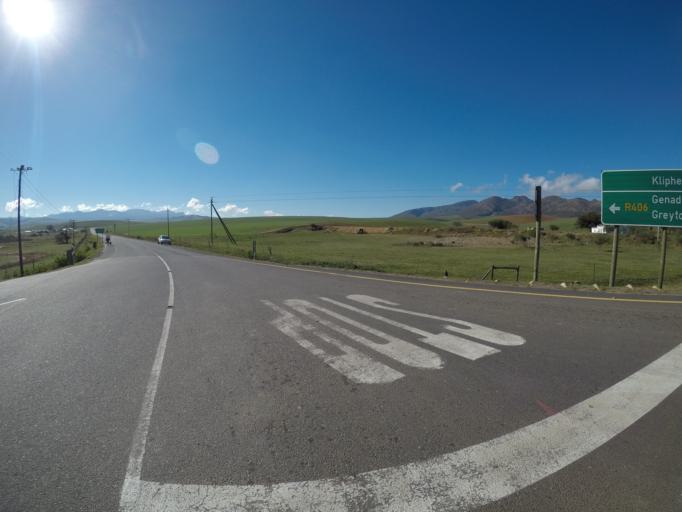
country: ZA
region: Western Cape
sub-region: Overberg District Municipality
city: Caledon
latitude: -34.2113
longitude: 19.3986
